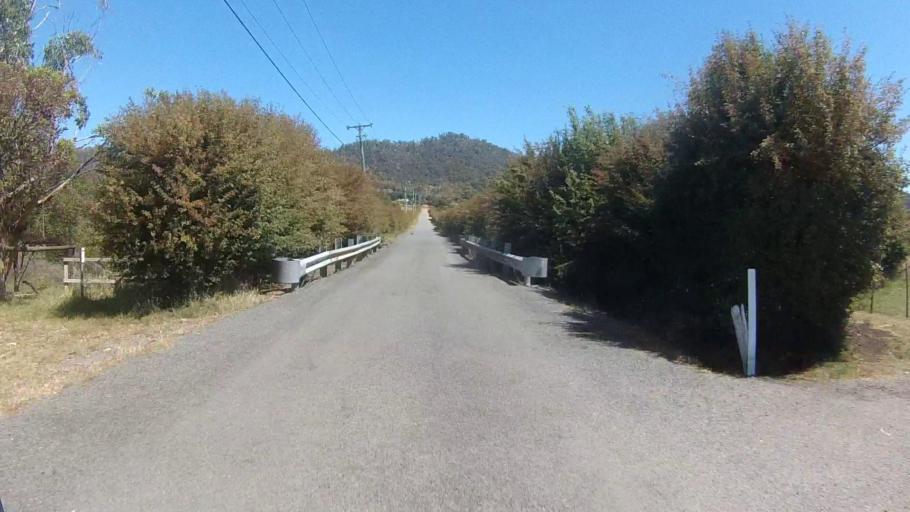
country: AU
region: Tasmania
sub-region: Clarence
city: Cambridge
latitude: -42.8438
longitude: 147.4595
